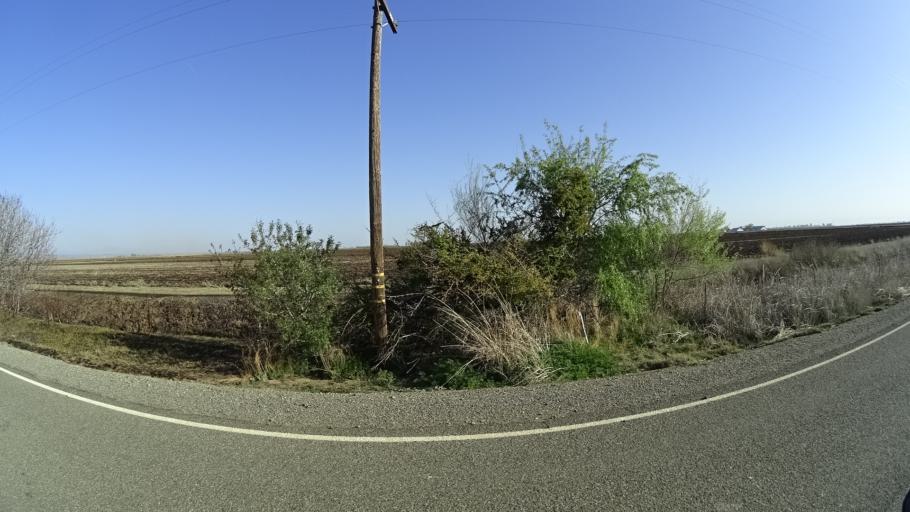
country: US
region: California
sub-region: Glenn County
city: Willows
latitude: 39.4071
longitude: -122.2207
